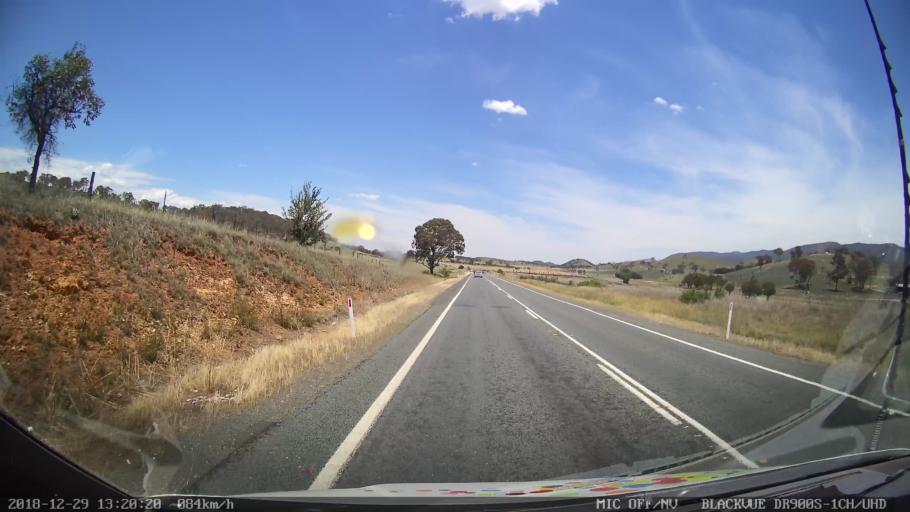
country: AU
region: Australian Capital Territory
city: Macarthur
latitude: -35.7774
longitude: 149.1619
